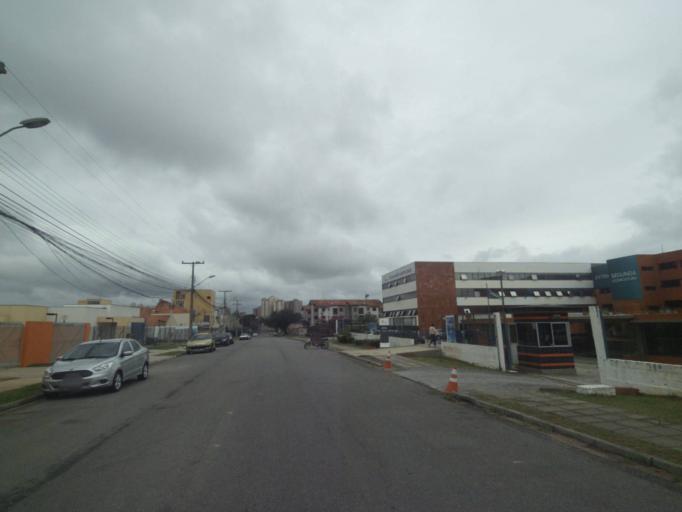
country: BR
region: Parana
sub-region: Curitiba
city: Curitiba
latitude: -25.4955
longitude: -49.3035
